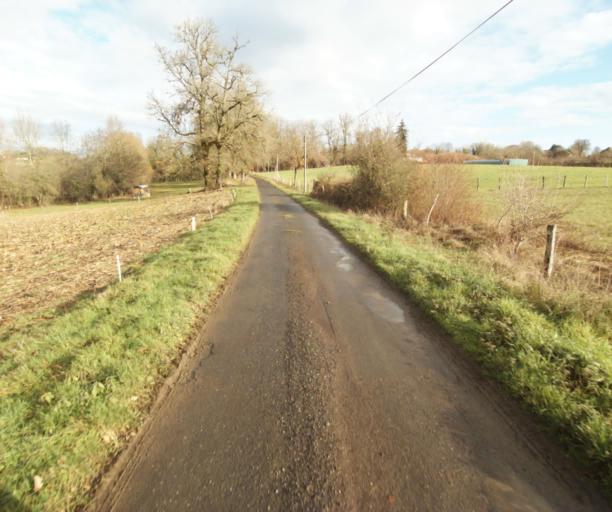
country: FR
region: Limousin
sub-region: Departement de la Correze
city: Sainte-Fereole
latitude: 45.2602
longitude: 1.5984
